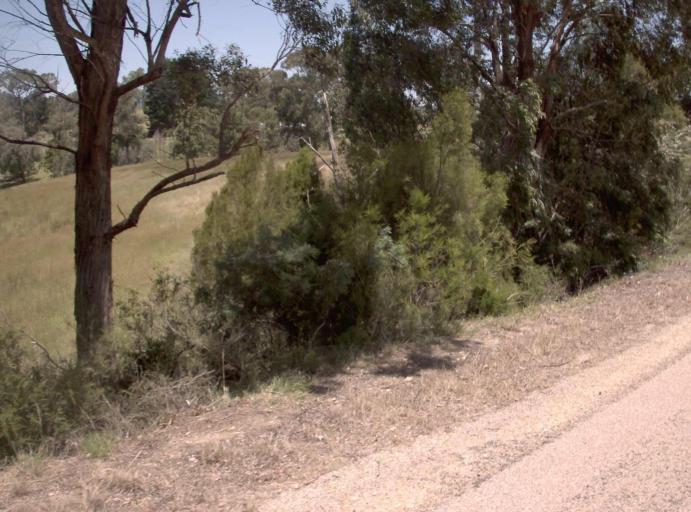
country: AU
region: Victoria
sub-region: East Gippsland
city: Bairnsdale
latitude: -37.7270
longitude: 147.7960
